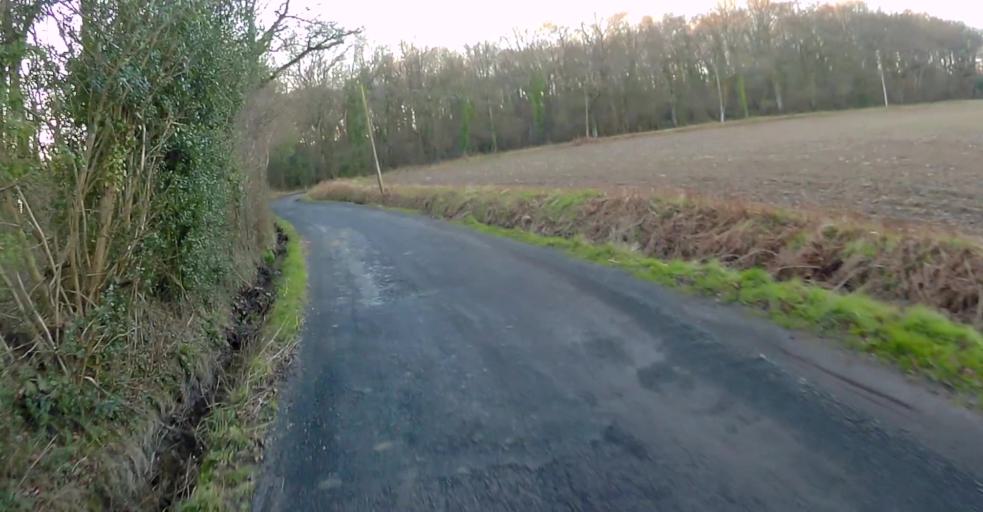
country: GB
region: England
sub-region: Hampshire
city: Hook
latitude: 51.3206
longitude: -0.9773
